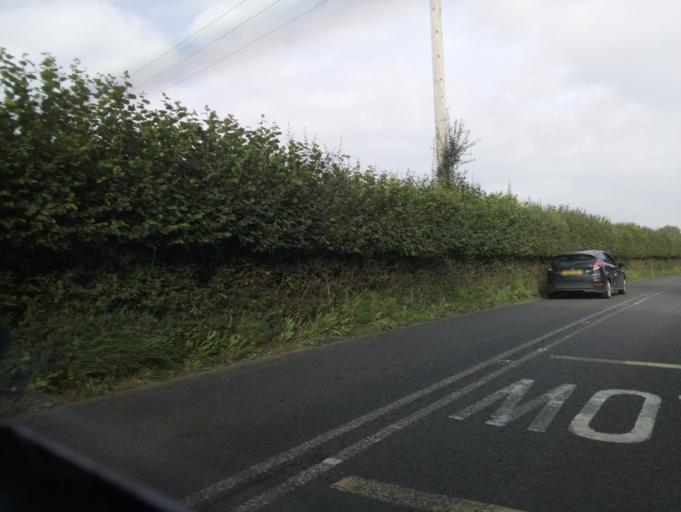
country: GB
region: England
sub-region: North Somerset
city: Winford
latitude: 51.3715
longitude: -2.6419
